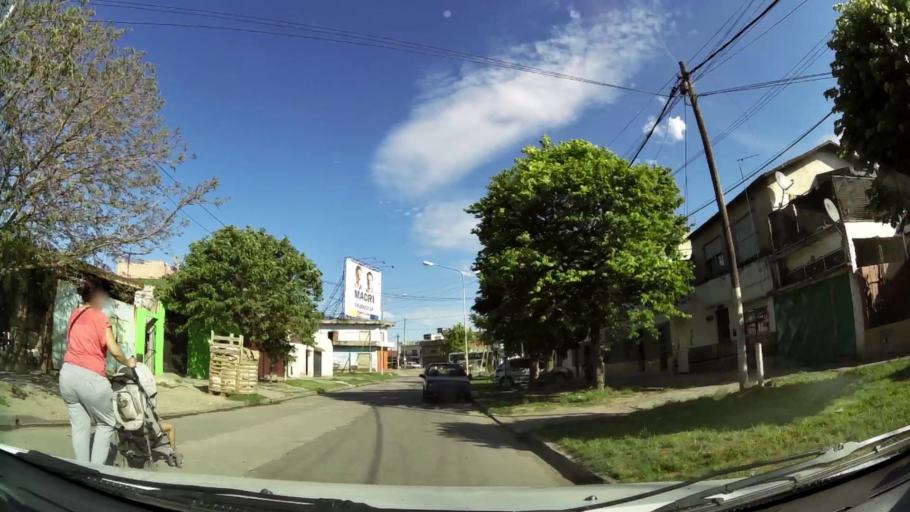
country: AR
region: Buenos Aires
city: Hurlingham
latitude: -34.5618
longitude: -58.6248
